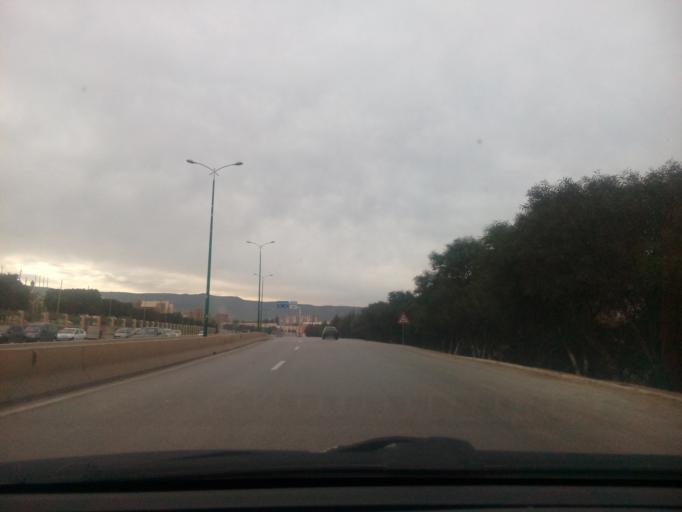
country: DZ
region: Tlemcen
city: Mansoura
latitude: 34.8963
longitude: -1.3555
